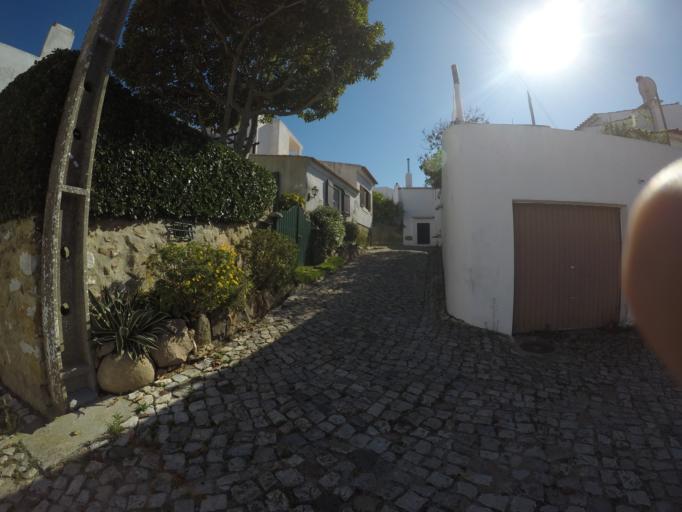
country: PT
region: Lisbon
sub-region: Sintra
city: Colares
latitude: 38.7865
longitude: -9.4764
